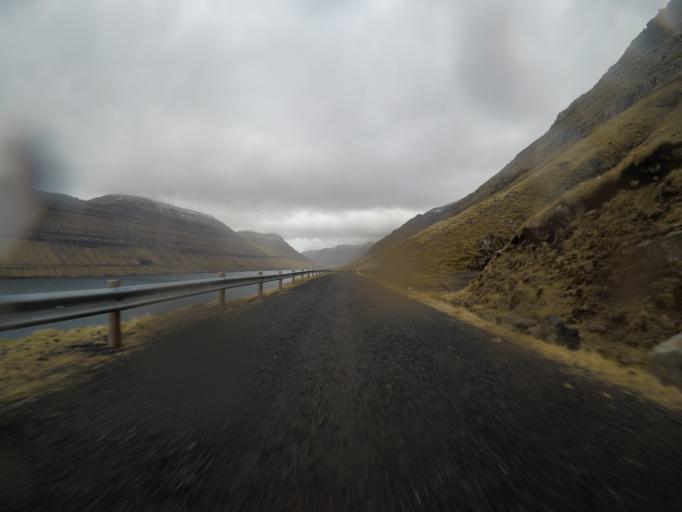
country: FO
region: Nordoyar
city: Klaksvik
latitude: 62.3288
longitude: -6.5692
